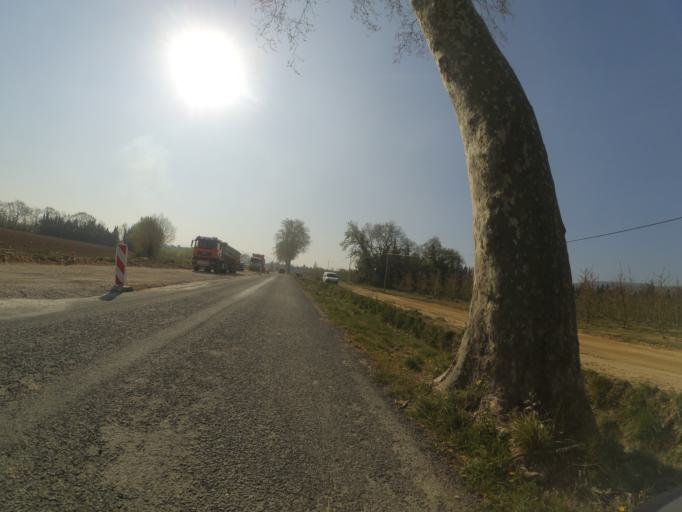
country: FR
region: Languedoc-Roussillon
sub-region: Departement des Pyrenees-Orientales
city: Thuir
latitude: 42.6480
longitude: 2.7362
